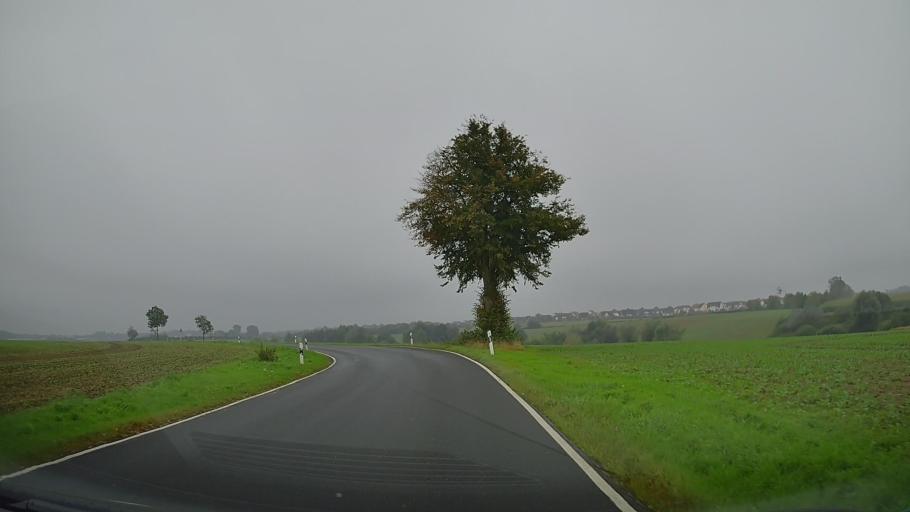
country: DE
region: Mecklenburg-Vorpommern
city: Wismar
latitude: 53.9149
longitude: 11.3954
